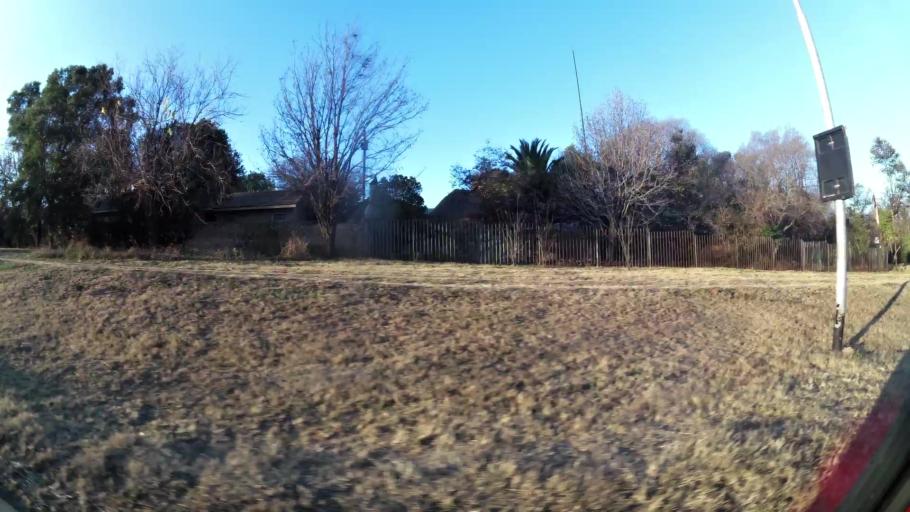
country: ZA
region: Gauteng
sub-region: City of Johannesburg Metropolitan Municipality
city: Midrand
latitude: -26.0006
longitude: 28.1125
